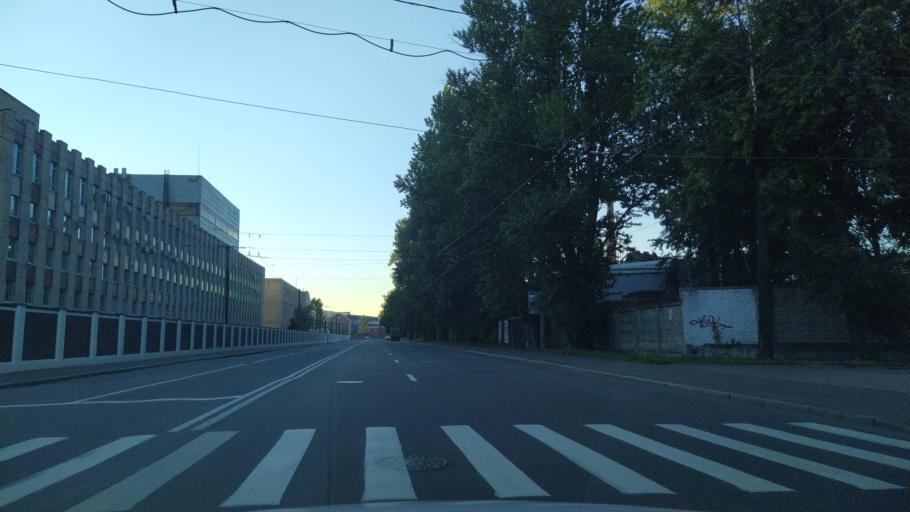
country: RU
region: Leningrad
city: Finlyandskiy
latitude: 59.9571
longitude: 30.3724
